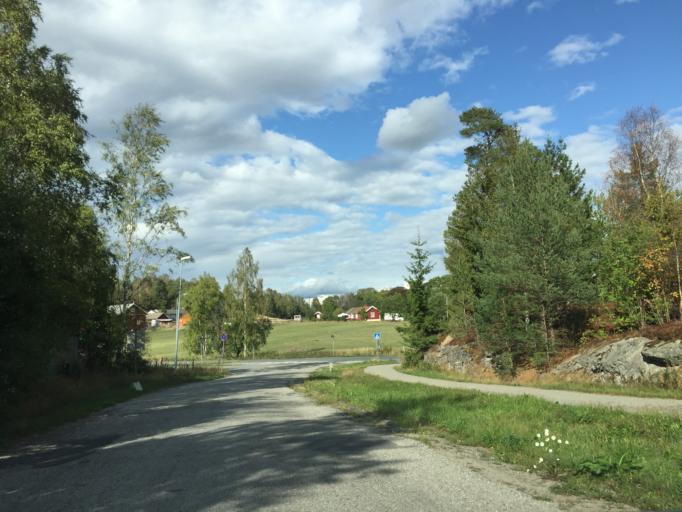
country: NO
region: Ostfold
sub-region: Askim
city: Askim
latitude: 59.5934
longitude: 11.1302
